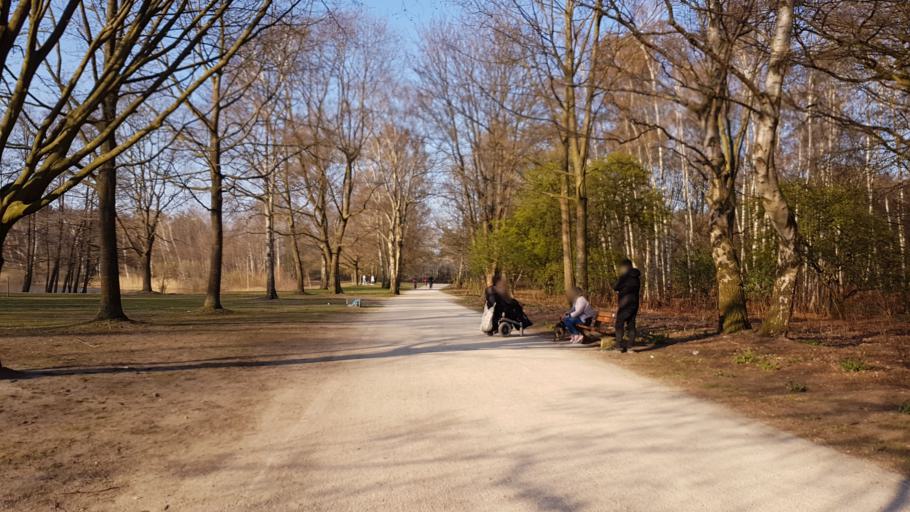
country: DE
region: Lower Saxony
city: Langenhagen
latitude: 52.4291
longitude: 9.7613
